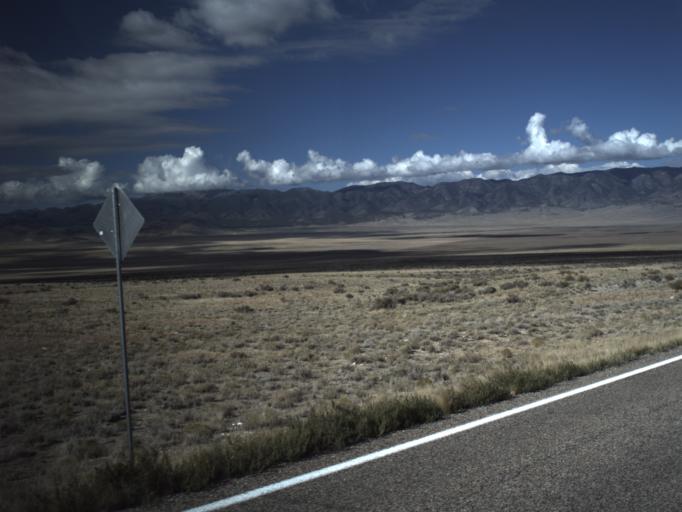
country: US
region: Utah
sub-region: Beaver County
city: Milford
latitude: 38.4388
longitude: -113.3130
